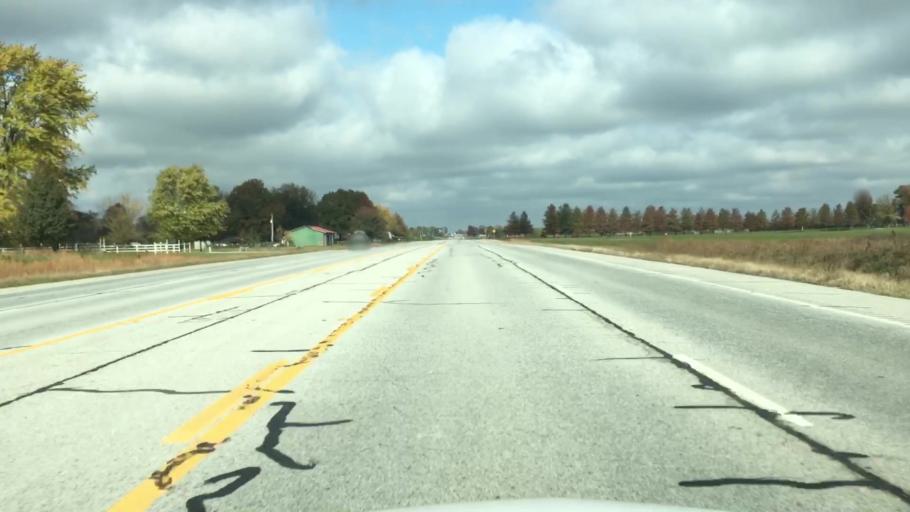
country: US
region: Arkansas
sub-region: Benton County
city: Siloam Springs
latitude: 36.2055
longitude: -94.4958
